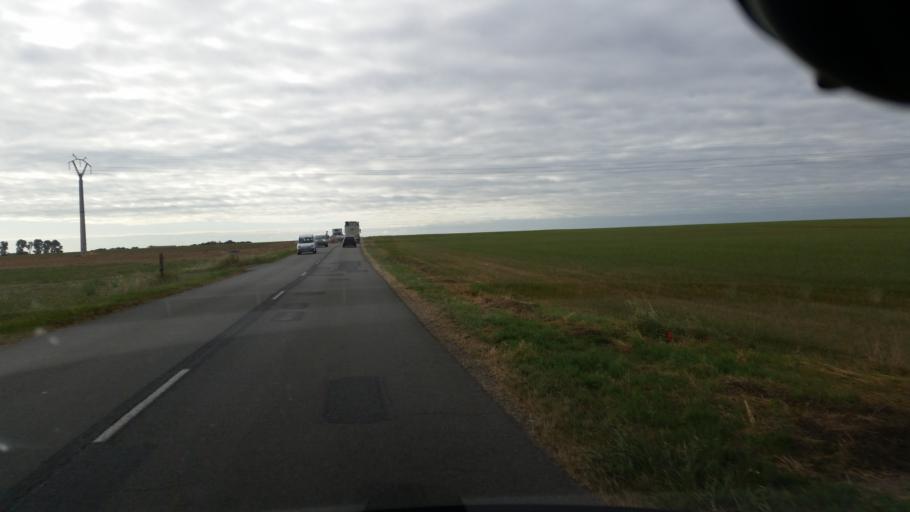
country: FR
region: Poitou-Charentes
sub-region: Departement de la Charente-Maritime
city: Marans
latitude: 46.2972
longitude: -0.9736
